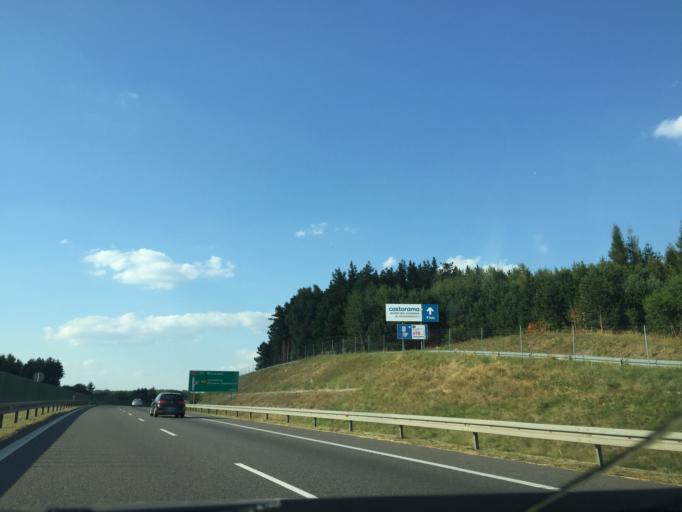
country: PL
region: Swietokrzyskie
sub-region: Powiat skarzyski
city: Suchedniow
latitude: 51.0392
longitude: 20.8202
